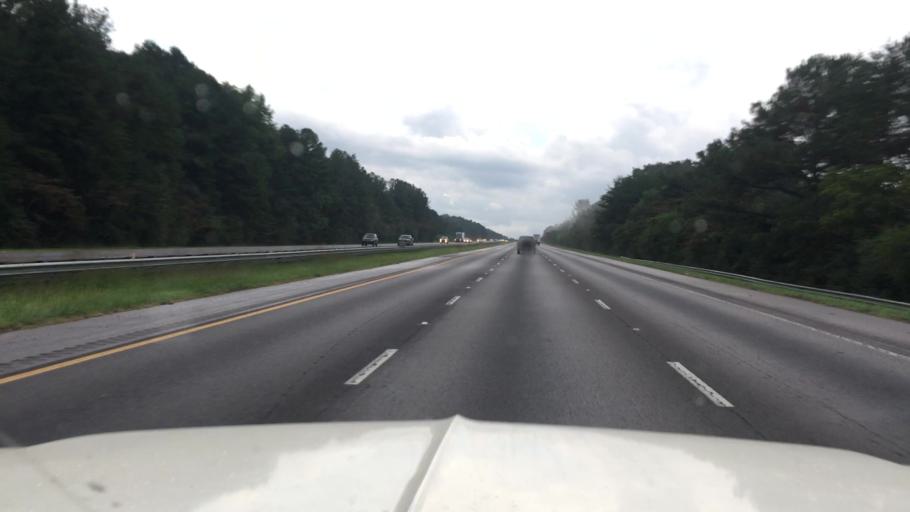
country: US
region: Alabama
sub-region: Jefferson County
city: Mount Olive
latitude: 33.6952
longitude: -86.8337
